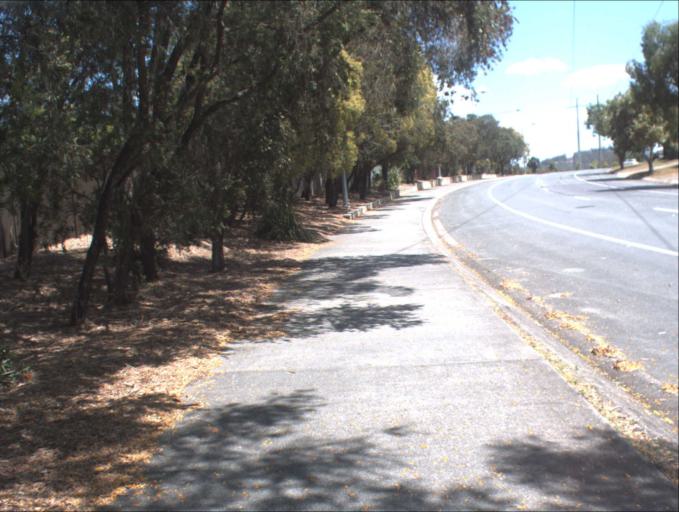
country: AU
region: Queensland
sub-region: Logan
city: Windaroo
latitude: -27.7453
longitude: 153.1924
